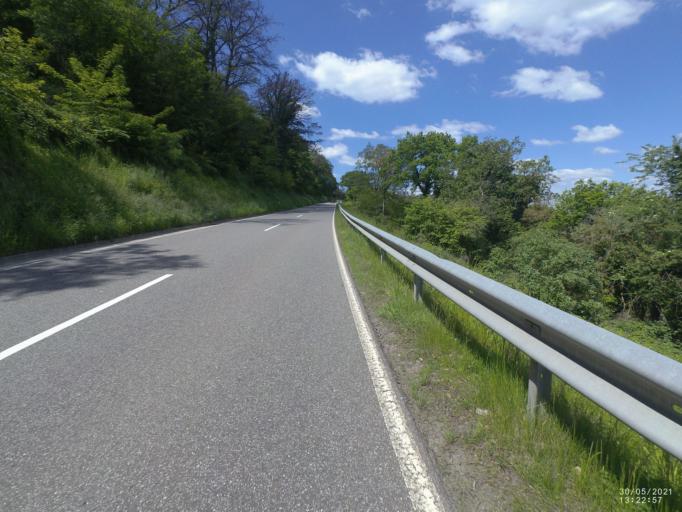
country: DE
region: Rheinland-Pfalz
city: Rhens
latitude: 50.2847
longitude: 7.6095
